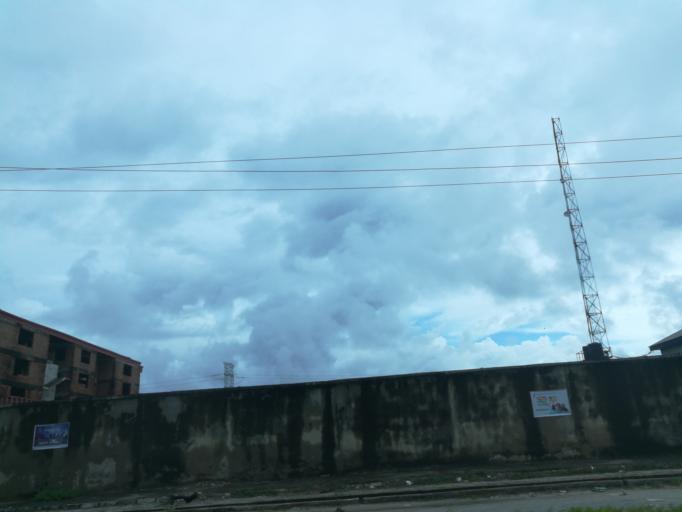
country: NG
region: Lagos
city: Ikoyi
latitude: 6.4318
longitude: 3.4616
